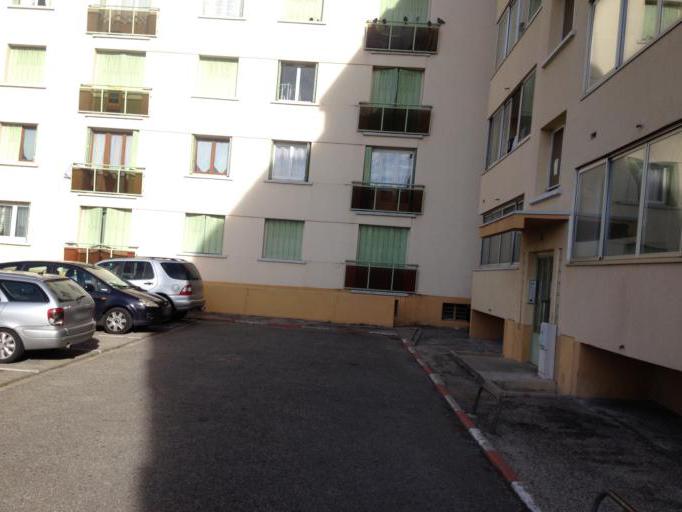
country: FR
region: Provence-Alpes-Cote d'Azur
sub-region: Departement du Vaucluse
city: Orange
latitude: 44.1295
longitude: 4.8024
